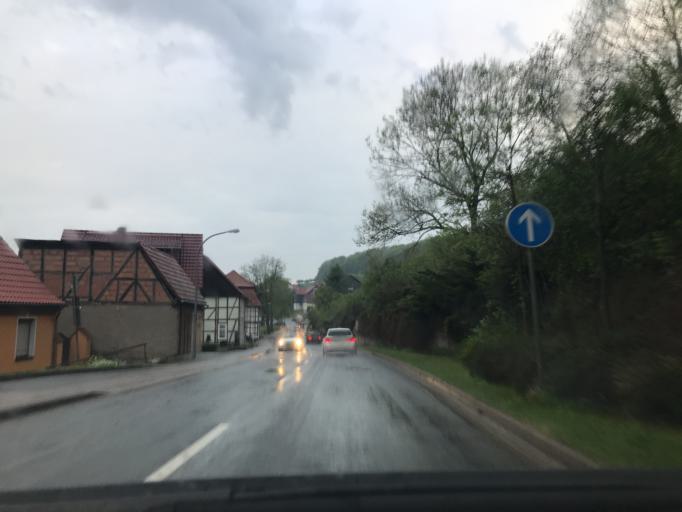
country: DE
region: Thuringia
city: Geisleden
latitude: 51.3513
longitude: 10.1972
